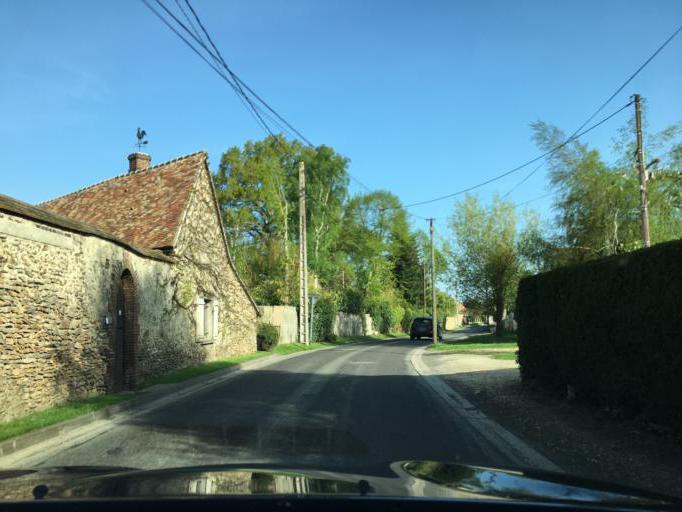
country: FR
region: Ile-de-France
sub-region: Departement des Yvelines
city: Conde-sur-Vesgre
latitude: 48.7399
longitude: 1.6688
